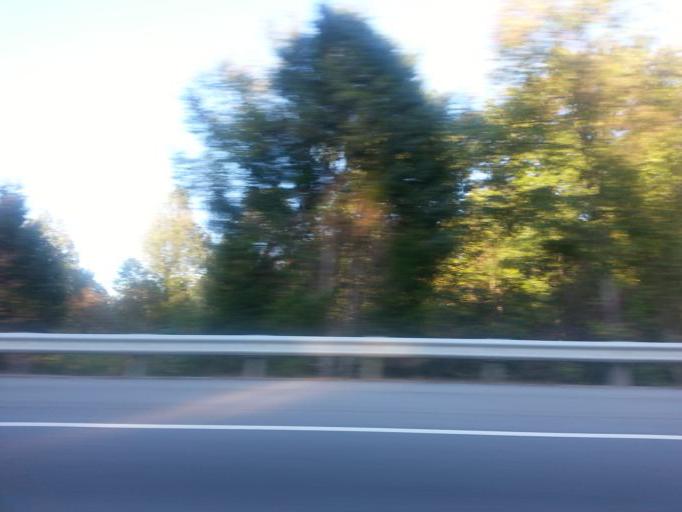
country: US
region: Tennessee
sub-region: Anderson County
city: Norris
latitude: 36.1142
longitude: -84.0260
